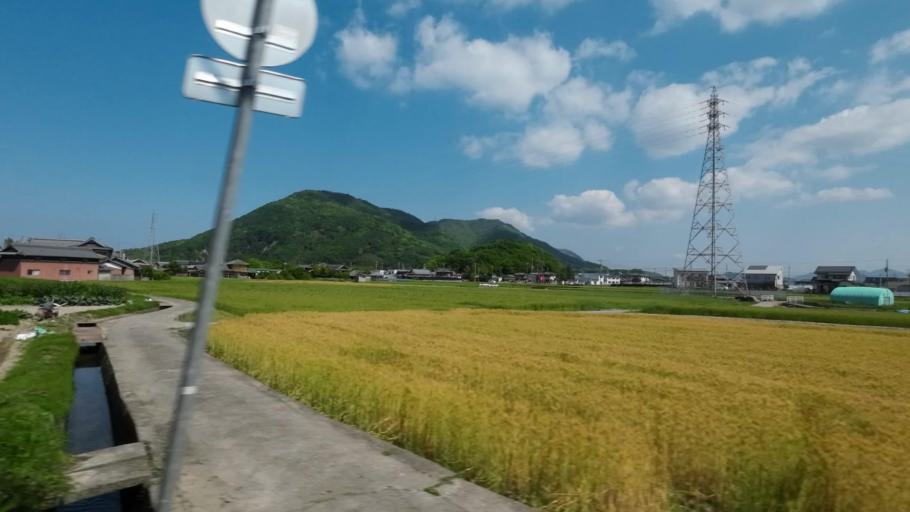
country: JP
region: Kagawa
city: Kan'onjicho
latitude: 34.1317
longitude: 133.6797
